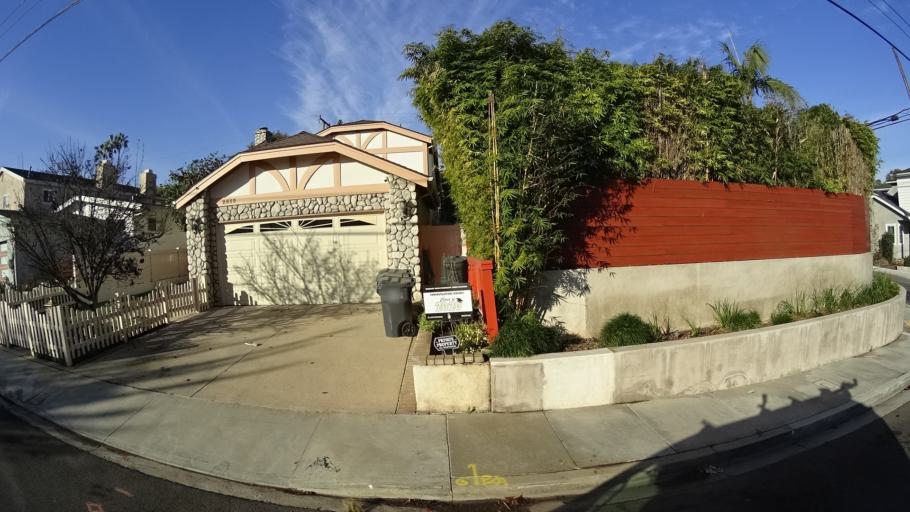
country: US
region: California
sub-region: Los Angeles County
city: Manhattan Beach
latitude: 33.8961
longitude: -118.4035
